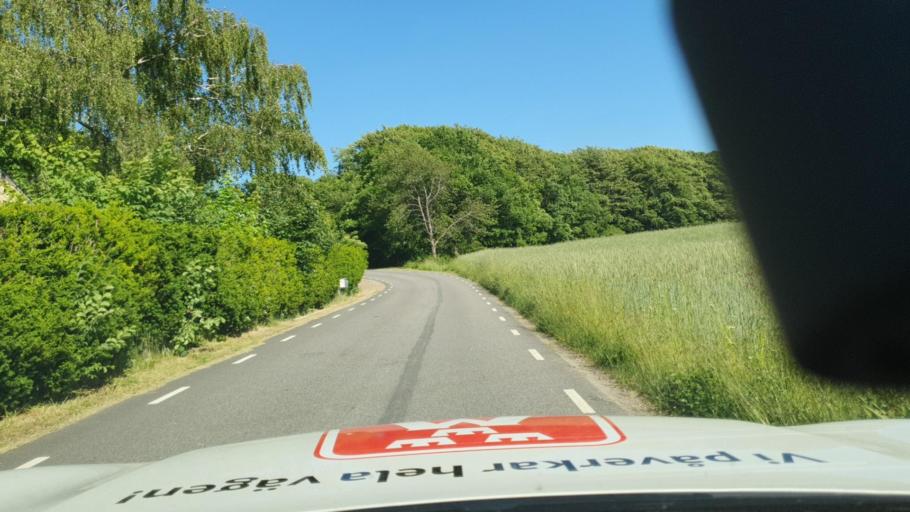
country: SE
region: Skane
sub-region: Sjobo Kommun
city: Sjoebo
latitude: 55.6487
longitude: 13.7648
